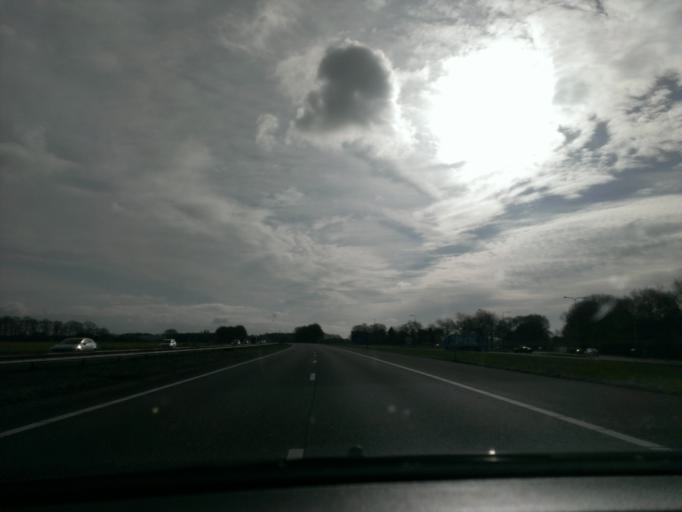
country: NL
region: Gelderland
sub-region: Gemeente Lochem
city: Laren
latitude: 52.2458
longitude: 6.3738
